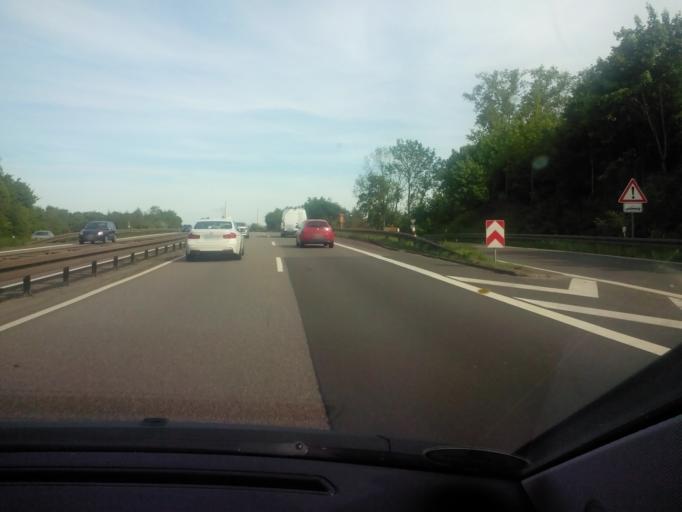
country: DE
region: Saarland
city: Saarlouis
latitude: 49.3055
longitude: 6.7371
